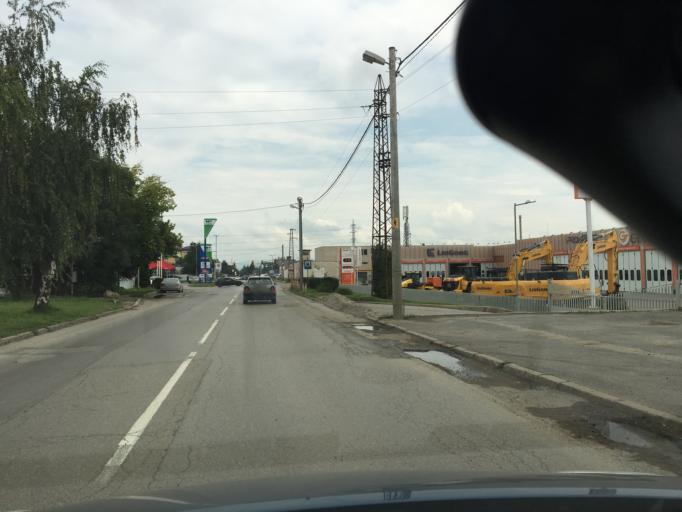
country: BG
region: Sofia-Capital
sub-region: Stolichna Obshtina
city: Sofia
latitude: 42.6204
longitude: 23.4038
